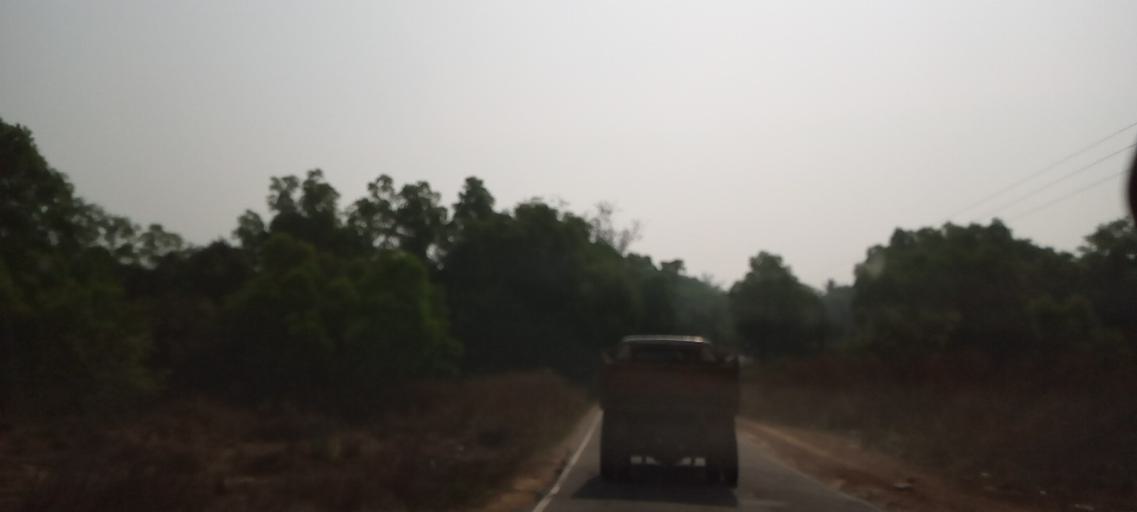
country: IN
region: Karnataka
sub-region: Udupi
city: Coondapoor
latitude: 13.5170
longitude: 74.7643
